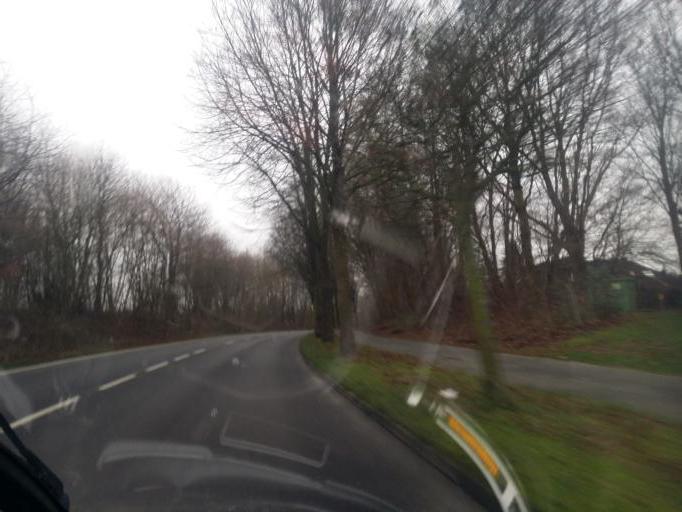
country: DE
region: Schleswig-Holstein
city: Heide
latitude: 54.2018
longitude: 9.1229
